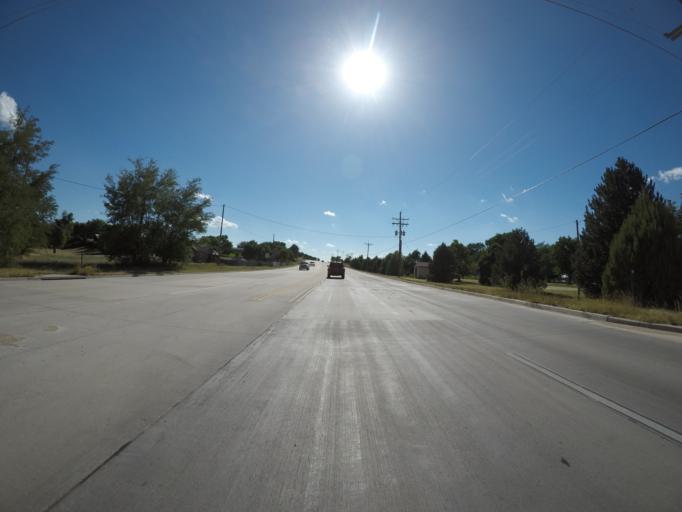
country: US
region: Colorado
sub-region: Logan County
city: Sterling
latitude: 40.6247
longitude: -103.2462
